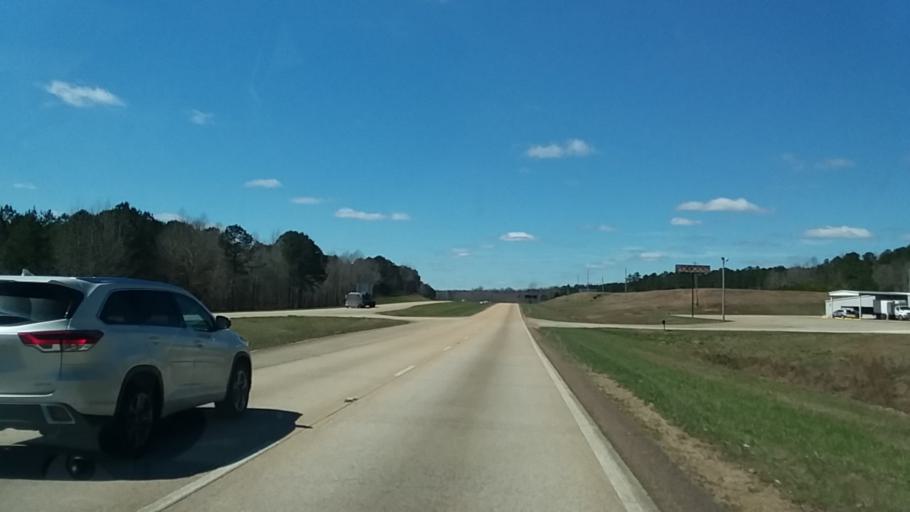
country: US
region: Mississippi
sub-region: Tishomingo County
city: Iuka
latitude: 34.7994
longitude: -88.2243
